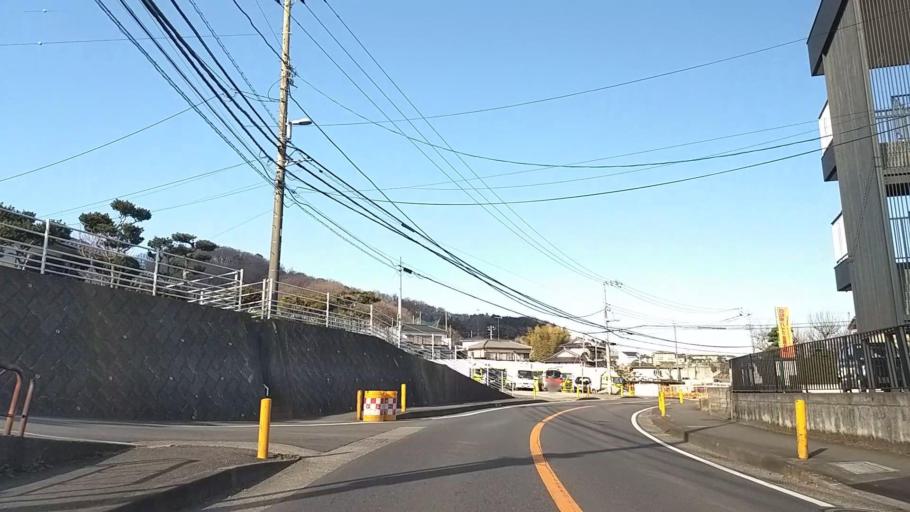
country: JP
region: Kanagawa
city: Atsugi
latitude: 35.4384
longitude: 139.3233
